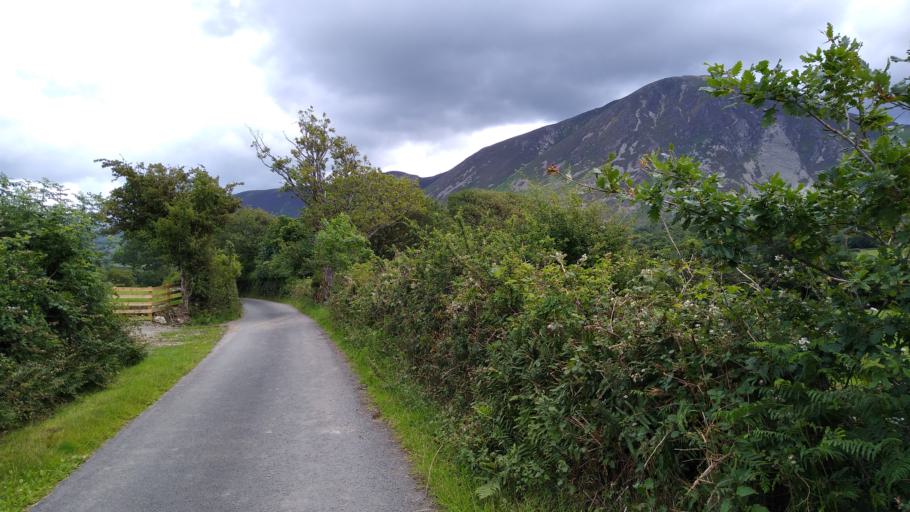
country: GB
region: England
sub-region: Cumbria
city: Cockermouth
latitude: 54.5838
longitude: -3.3255
